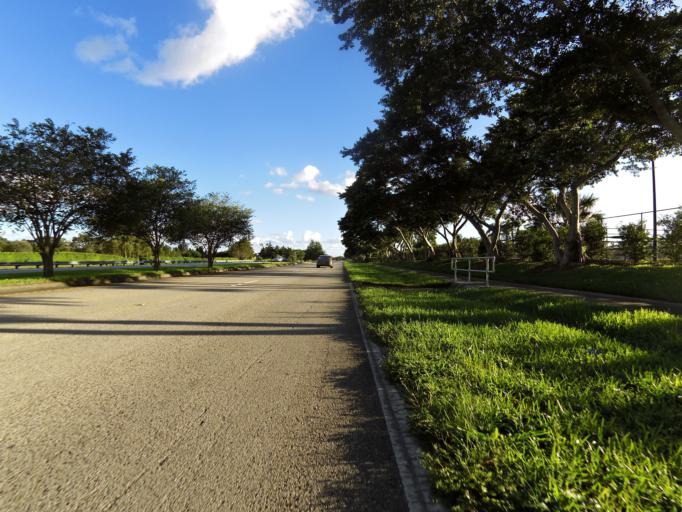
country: US
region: Florida
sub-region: Broward County
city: Pine Island Ridge
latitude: 26.0804
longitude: -80.2652
